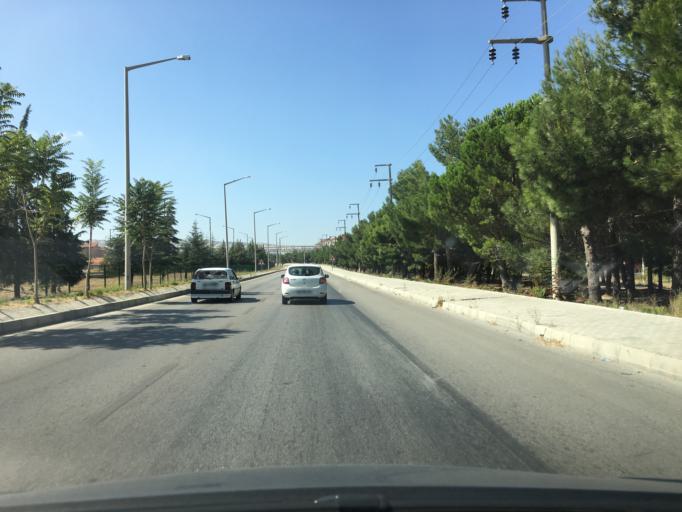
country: TR
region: Burdur
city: Burdur
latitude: 37.7295
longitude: 30.3044
